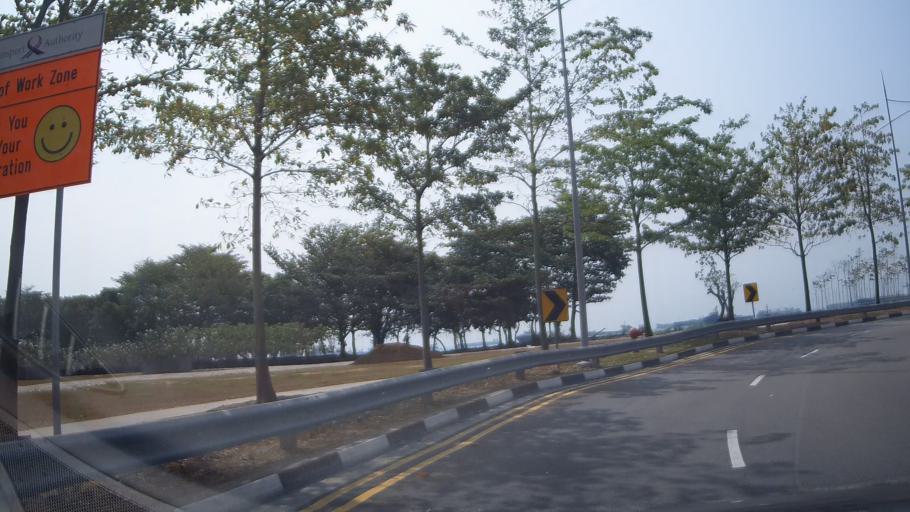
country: SG
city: Singapore
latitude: 1.2697
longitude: 103.8665
